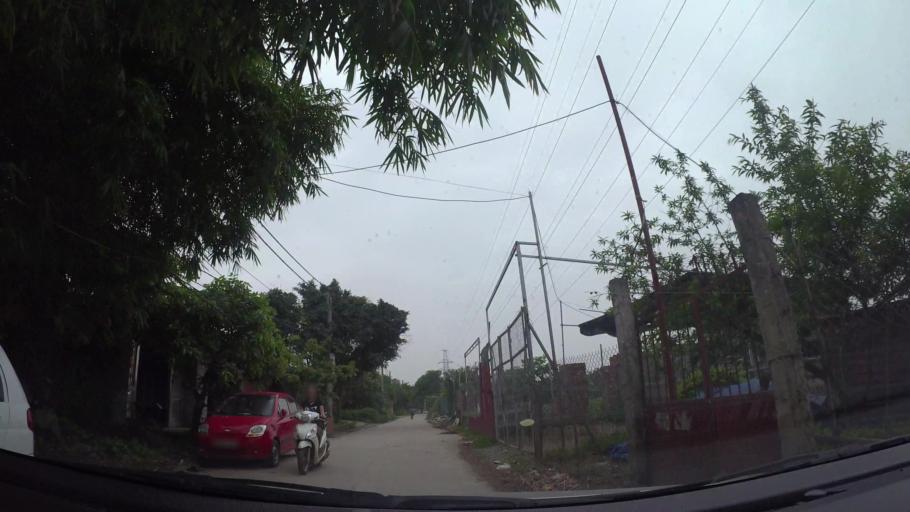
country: VN
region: Ha Noi
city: Tay Ho
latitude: 21.0591
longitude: 105.8397
